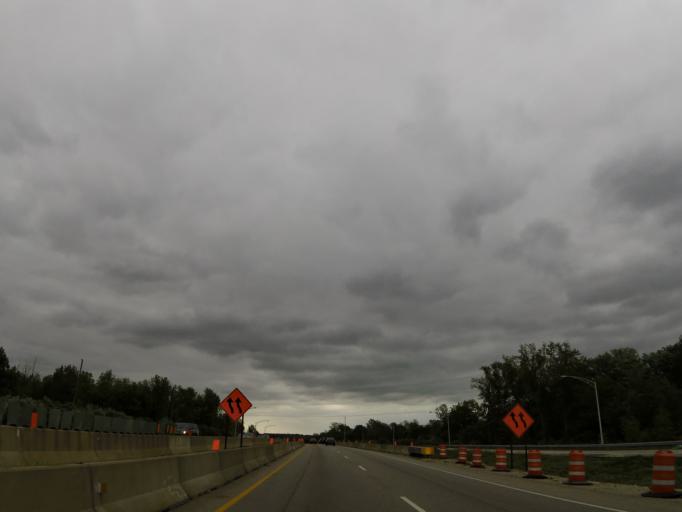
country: US
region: Ohio
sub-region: Warren County
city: Morrow
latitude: 39.4152
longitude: -84.1205
